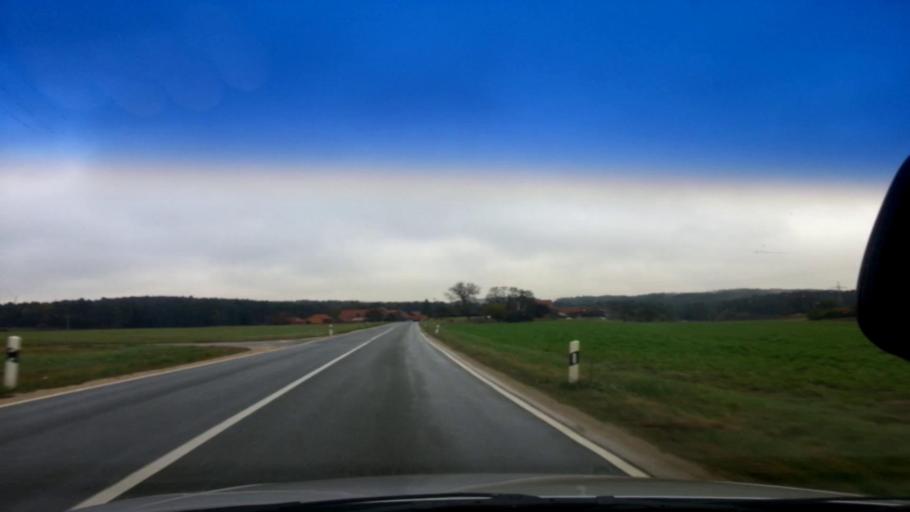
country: DE
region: Bavaria
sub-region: Upper Franconia
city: Wattendorf
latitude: 49.9914
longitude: 11.1255
